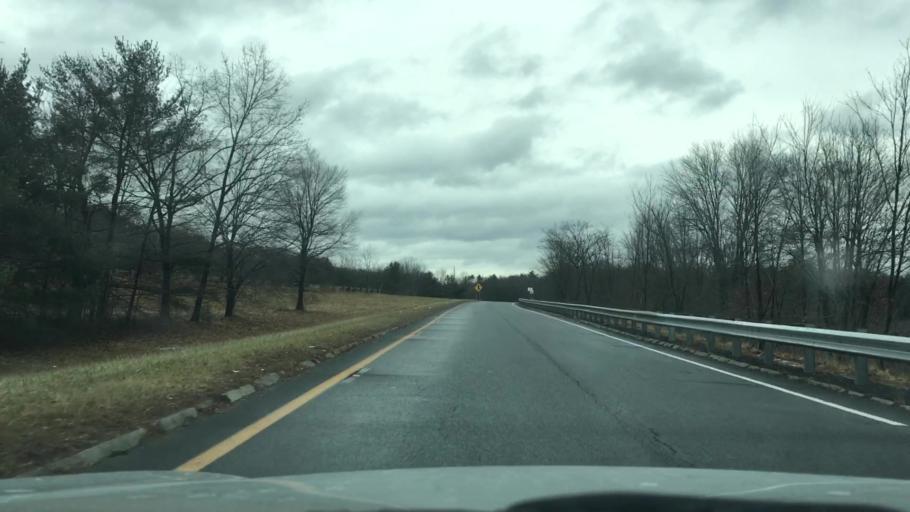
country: US
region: Massachusetts
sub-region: Franklin County
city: Greenfield
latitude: 42.6095
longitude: -72.5846
